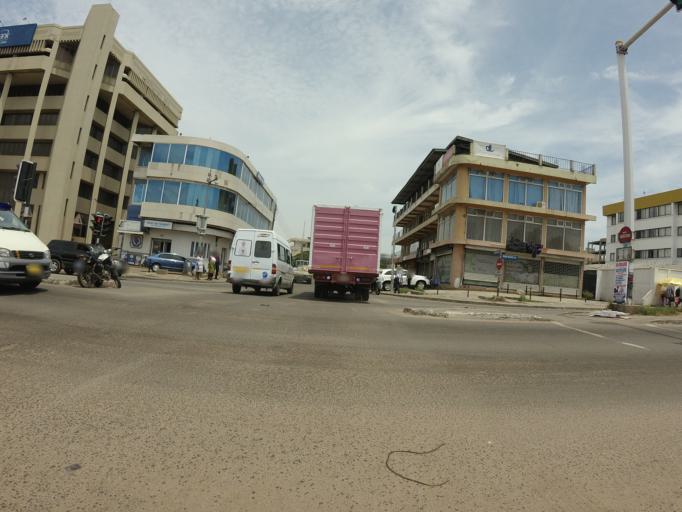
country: GH
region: Greater Accra
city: Accra
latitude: 5.5551
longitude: -0.2117
